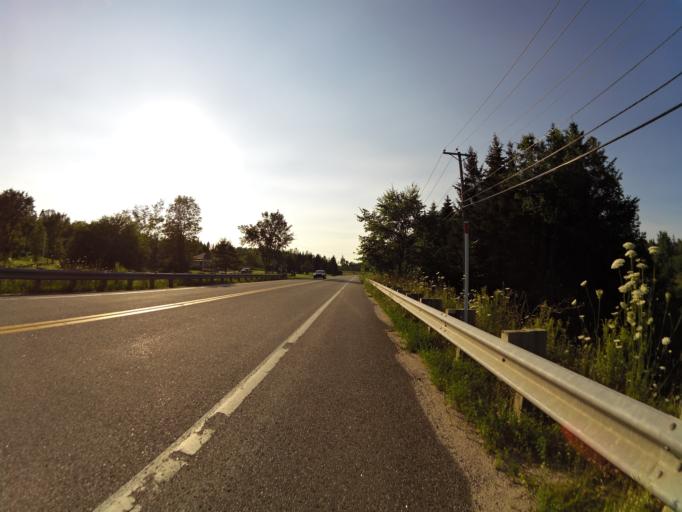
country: CA
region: Quebec
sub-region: Outaouais
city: Wakefield
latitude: 45.5814
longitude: -75.8834
